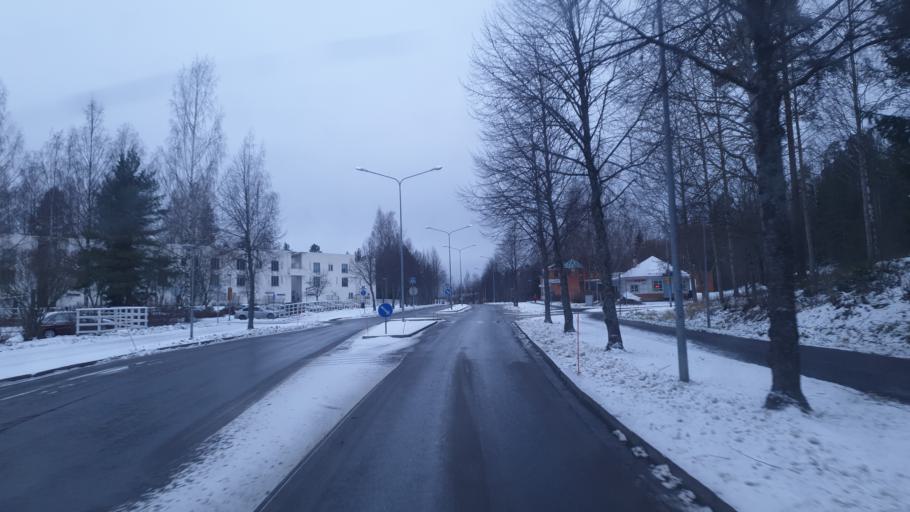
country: FI
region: Northern Savo
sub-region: Kuopio
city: Kuopio
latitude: 62.8355
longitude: 27.6260
